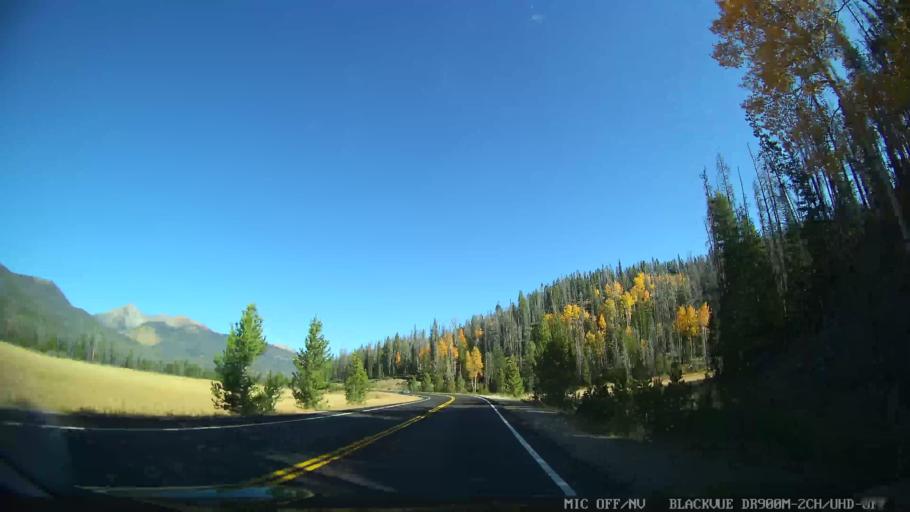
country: US
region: Colorado
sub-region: Grand County
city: Granby
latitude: 40.3272
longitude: -105.8539
